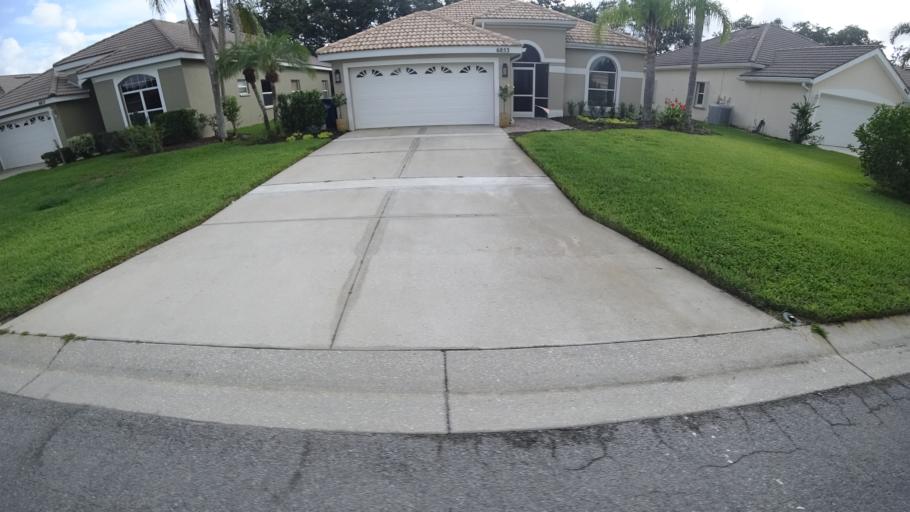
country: US
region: Florida
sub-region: Sarasota County
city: Desoto Lakes
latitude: 27.4193
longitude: -82.4825
